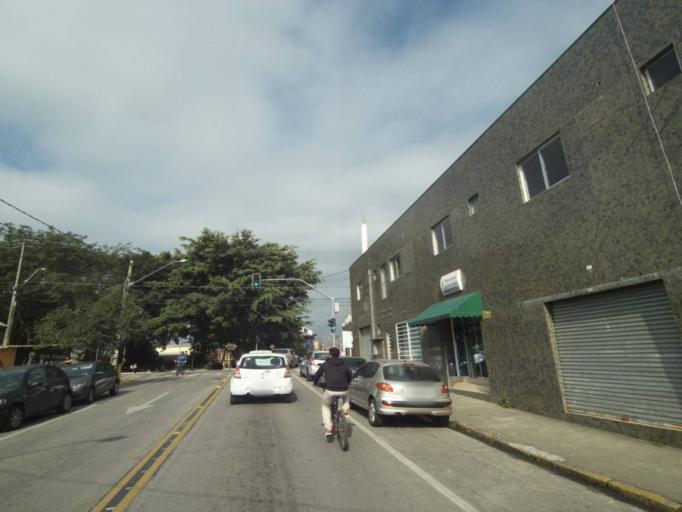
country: BR
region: Parana
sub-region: Paranagua
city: Paranagua
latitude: -25.5199
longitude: -48.5102
